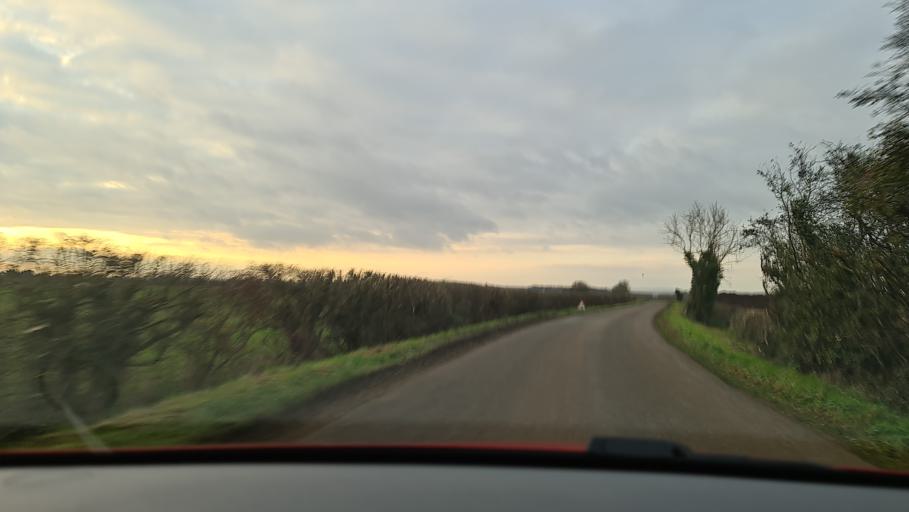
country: GB
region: England
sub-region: Oxfordshire
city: Somerton
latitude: 51.9201
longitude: -1.2733
